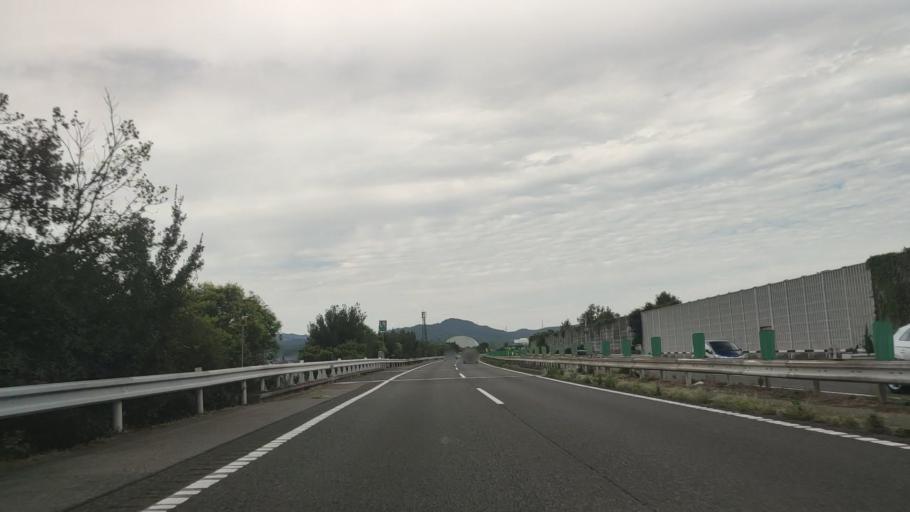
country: JP
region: Shiga Prefecture
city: Omihachiman
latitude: 35.0550
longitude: 136.1311
